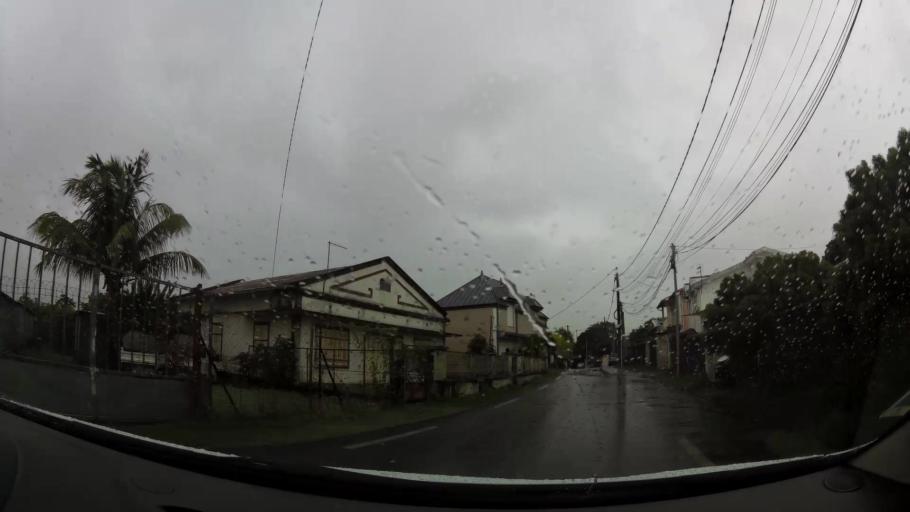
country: RE
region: Reunion
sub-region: Reunion
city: Saint-Andre
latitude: -20.9662
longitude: 55.6508
